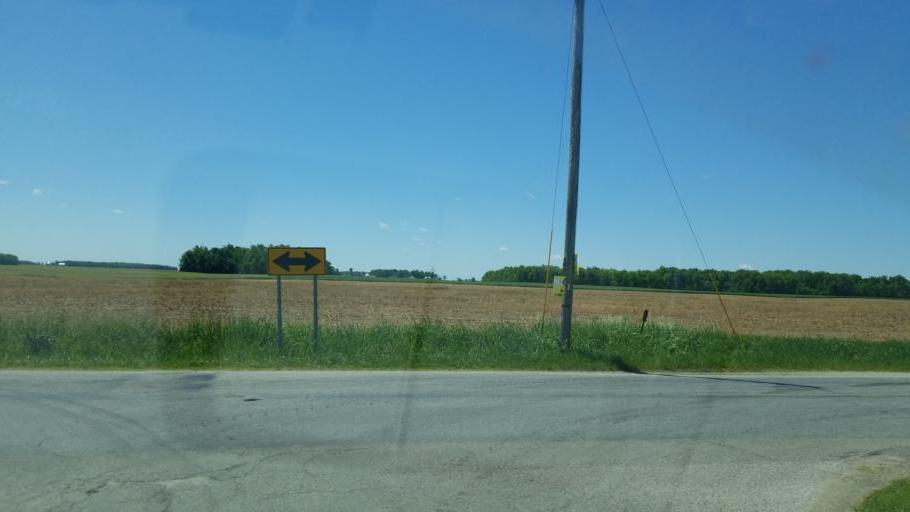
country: US
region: Ohio
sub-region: Shelby County
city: Fort Loramie
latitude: 40.3585
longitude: -84.2974
